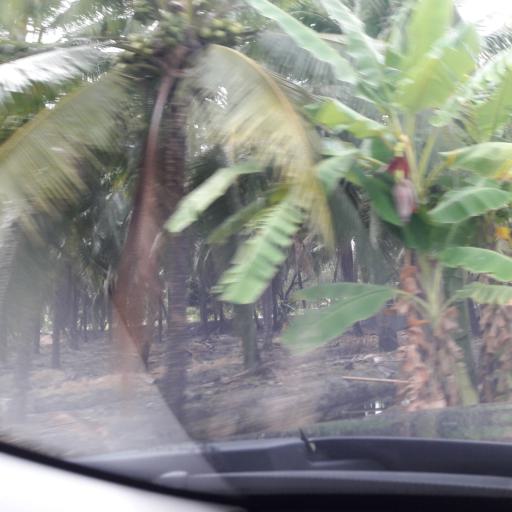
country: TH
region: Ratchaburi
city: Damnoen Saduak
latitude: 13.5661
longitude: 99.9573
